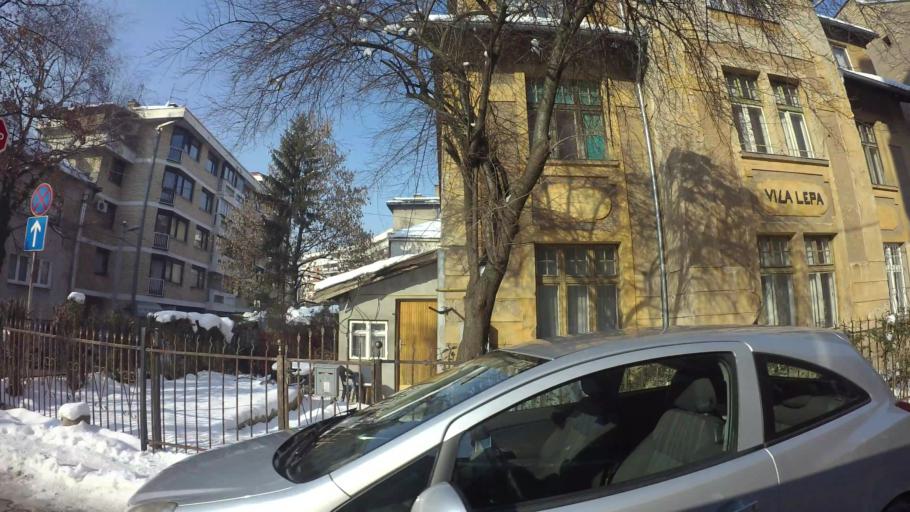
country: BA
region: Federation of Bosnia and Herzegovina
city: Kobilja Glava
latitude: 43.8517
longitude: 18.4041
